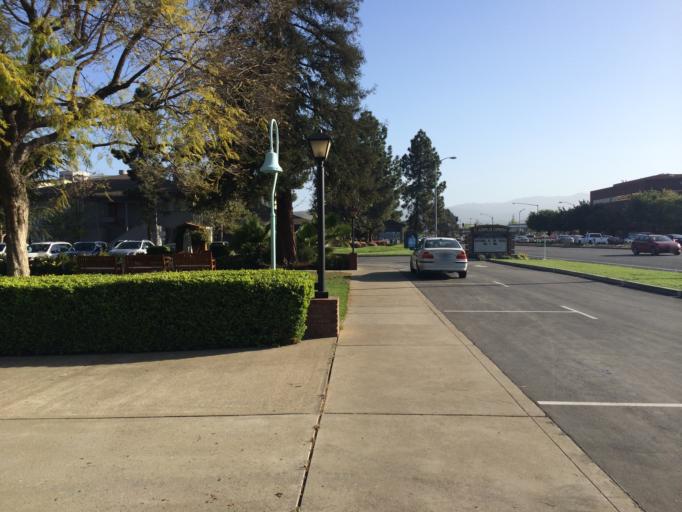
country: US
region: California
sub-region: Santa Clara County
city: Cupertino
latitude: 37.3247
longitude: -122.0320
